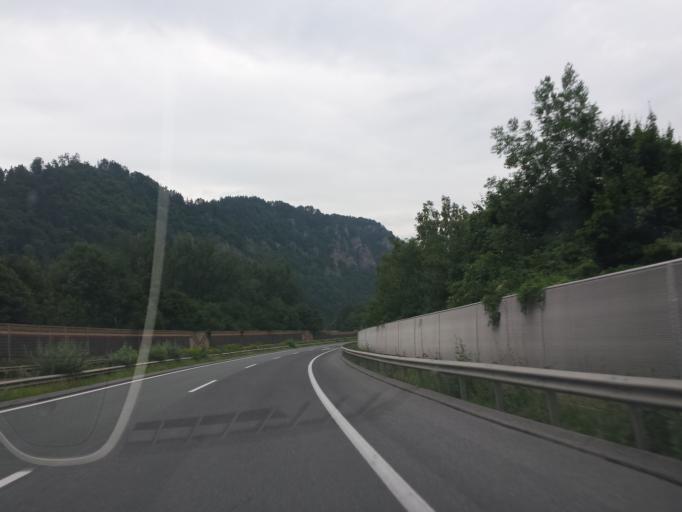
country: AT
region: Styria
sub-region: Politischer Bezirk Graz-Umgebung
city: Peggau
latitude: 47.2053
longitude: 15.3390
